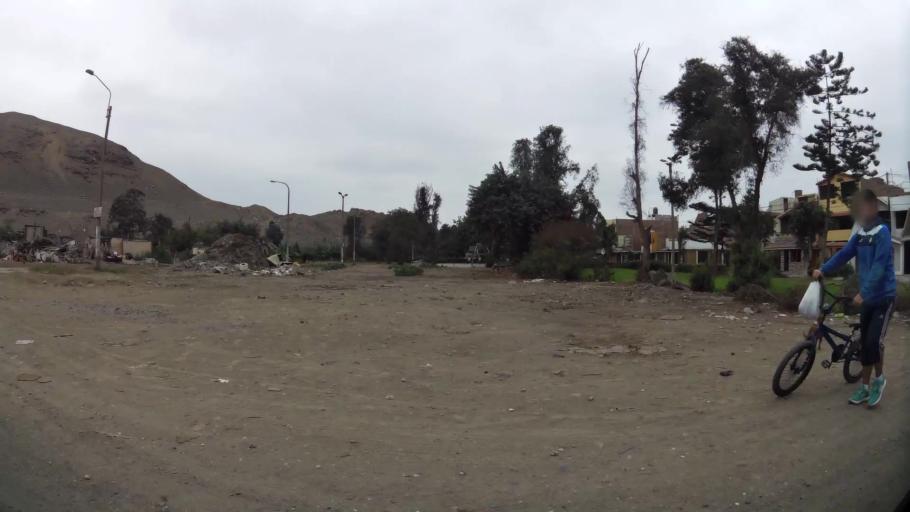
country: PE
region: Lima
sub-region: Lima
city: Independencia
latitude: -11.9388
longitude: -77.0838
